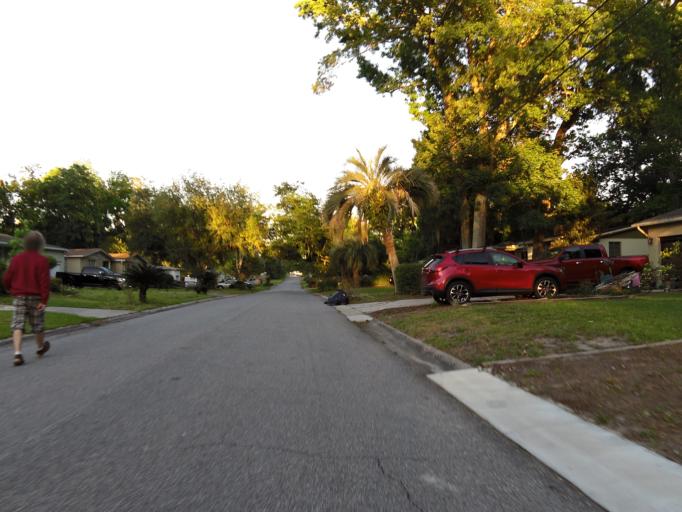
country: US
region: Florida
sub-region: Duval County
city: Jacksonville
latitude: 30.2587
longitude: -81.6420
